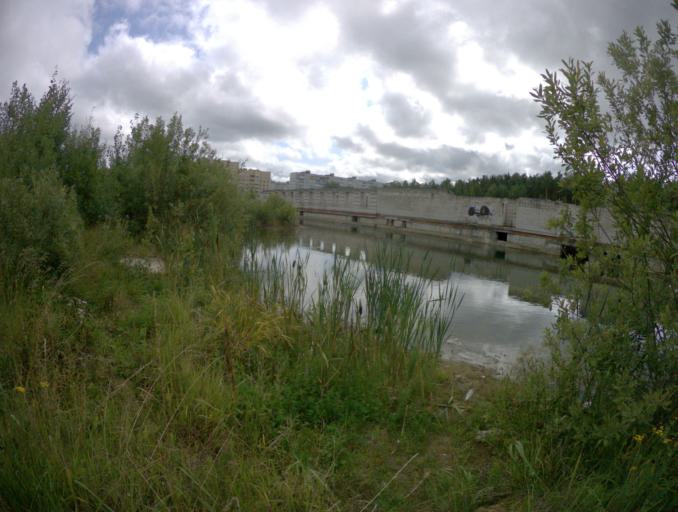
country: RU
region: Vladimir
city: Raduzhnyy
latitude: 56.0069
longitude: 40.3299
